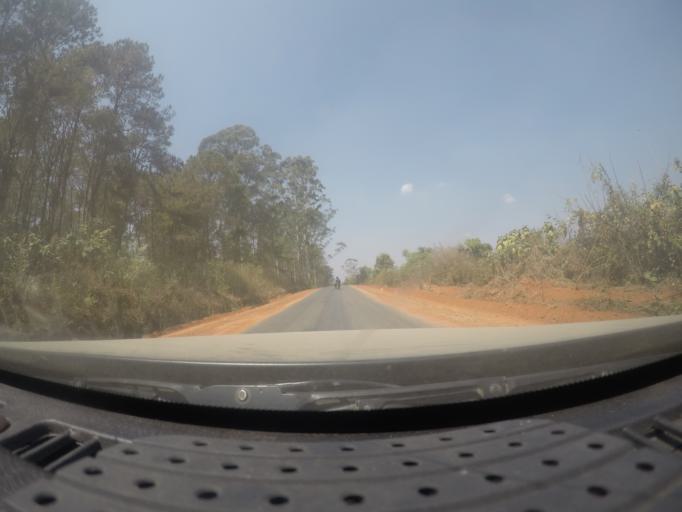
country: MM
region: Shan
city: Taunggyi
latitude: 20.9811
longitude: 96.5382
